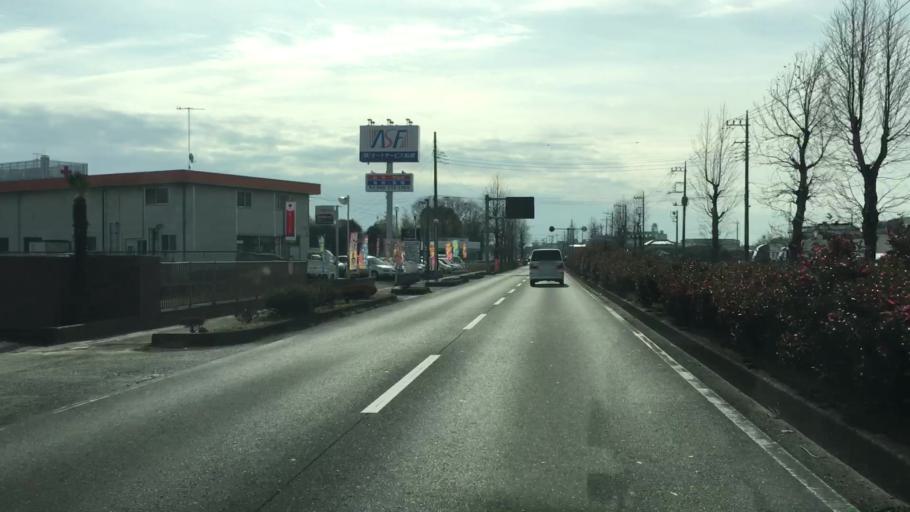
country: JP
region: Saitama
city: Menuma
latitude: 36.1809
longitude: 139.3701
